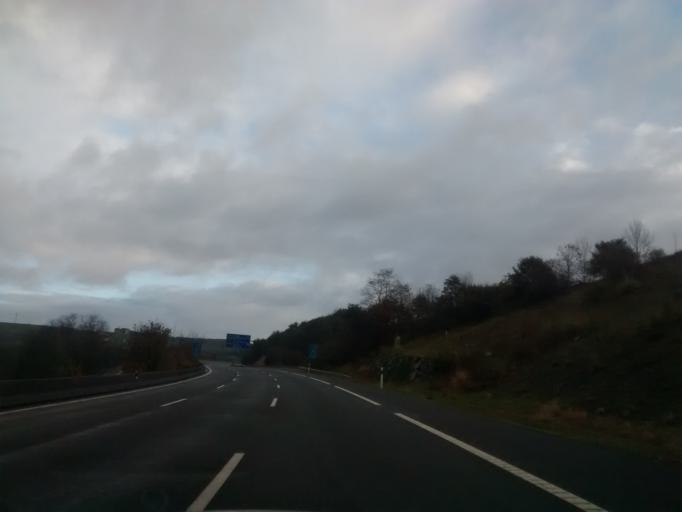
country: ES
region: Cantabria
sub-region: Provincia de Cantabria
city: Hazas de Cesto
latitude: 43.4130
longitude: -3.5591
